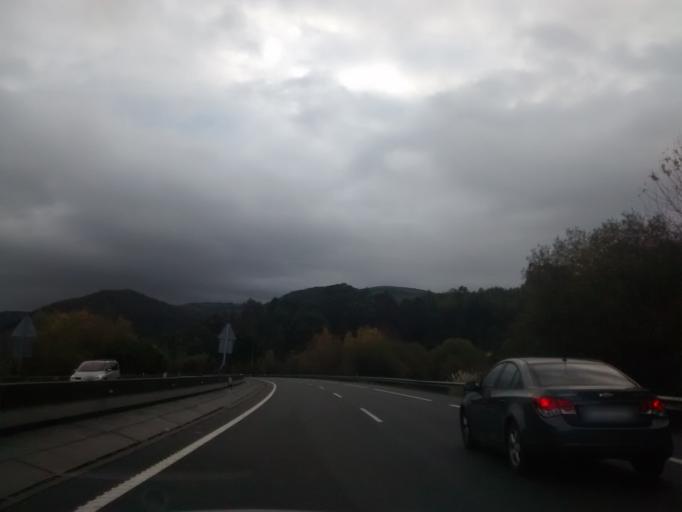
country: ES
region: Cantabria
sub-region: Provincia de Cantabria
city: Liendo
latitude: 43.3844
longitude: -3.3838
